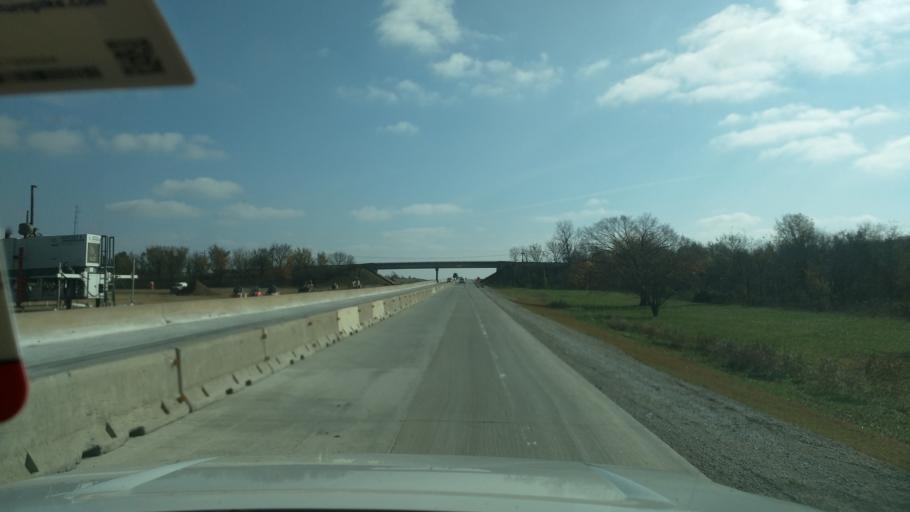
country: US
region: Oklahoma
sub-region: Wagoner County
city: Coweta
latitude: 36.0172
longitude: -95.6762
